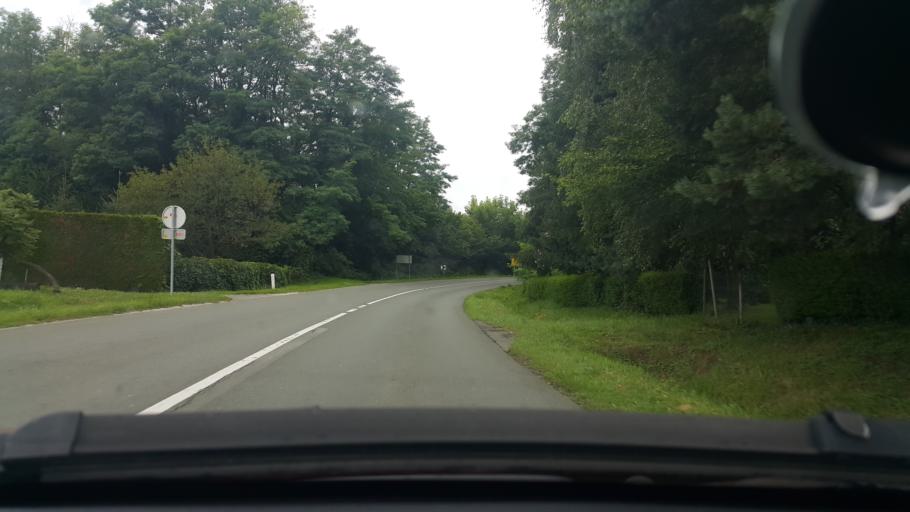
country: SI
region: Ormoz
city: Ormoz
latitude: 46.4066
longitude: 16.1338
